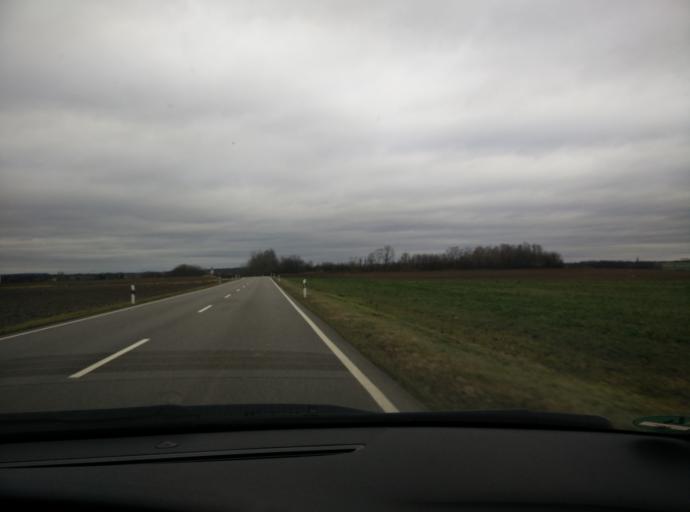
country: DE
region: Saxony
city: Frohburg
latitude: 51.0380
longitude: 12.5531
